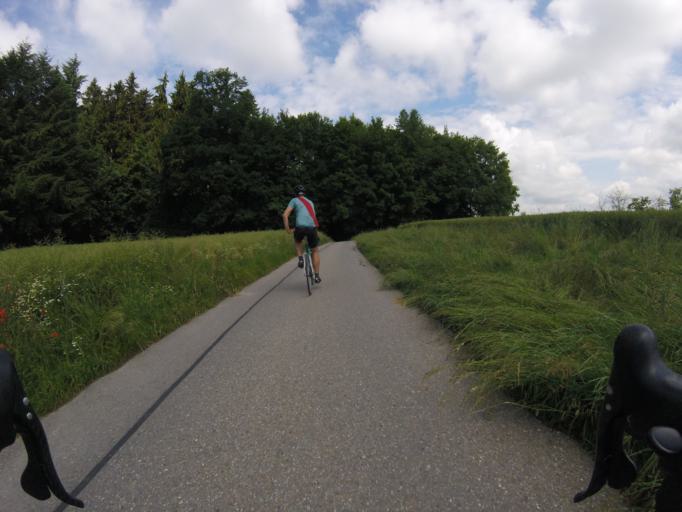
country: CH
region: Bern
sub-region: Bern-Mittelland District
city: Bariswil
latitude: 47.0179
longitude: 7.5171
